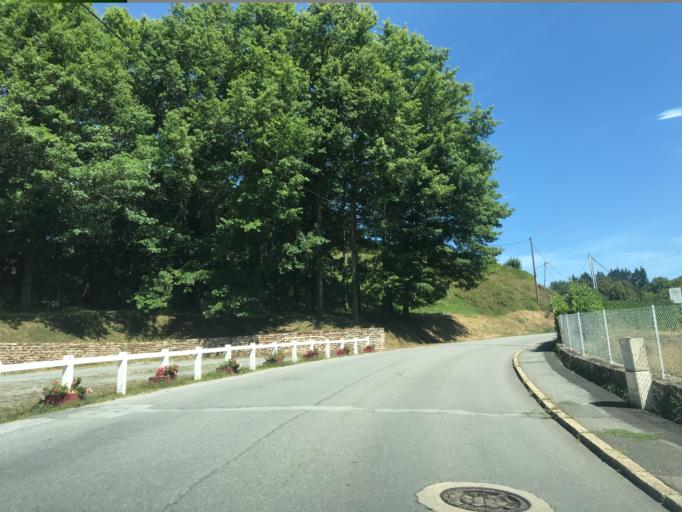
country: FR
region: Limousin
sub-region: Departement de la Creuse
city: Felletin
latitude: 45.8902
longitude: 2.1792
